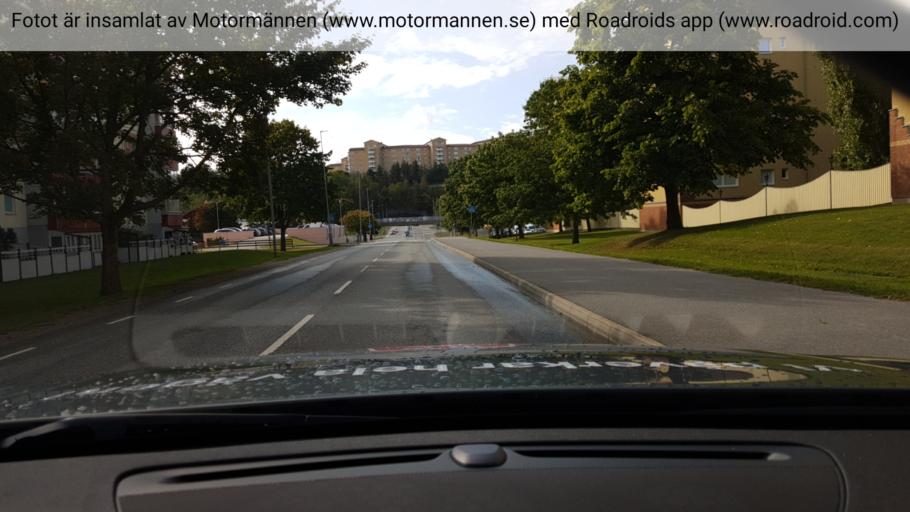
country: SE
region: Stockholm
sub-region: Botkyrka Kommun
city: Eriksberg
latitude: 59.2469
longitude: 17.8297
